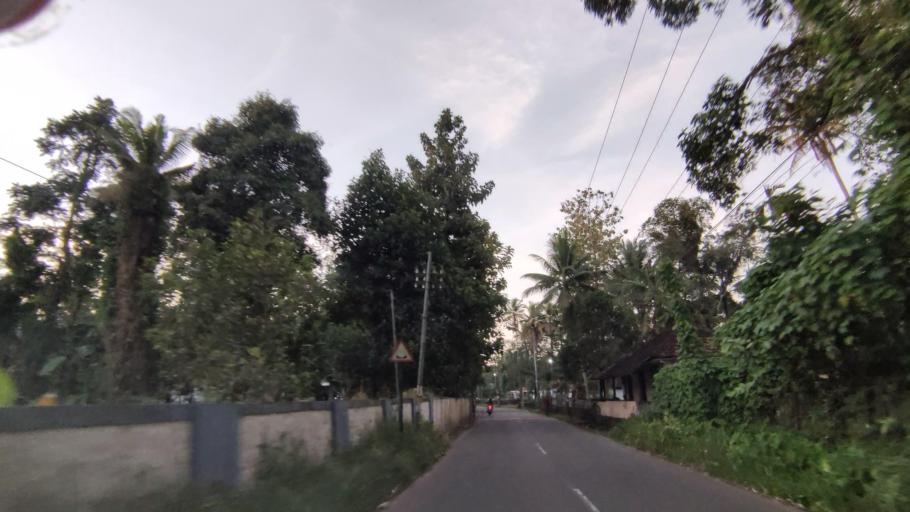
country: IN
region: Kerala
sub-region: Kottayam
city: Kottayam
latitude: 9.6669
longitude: 76.5072
